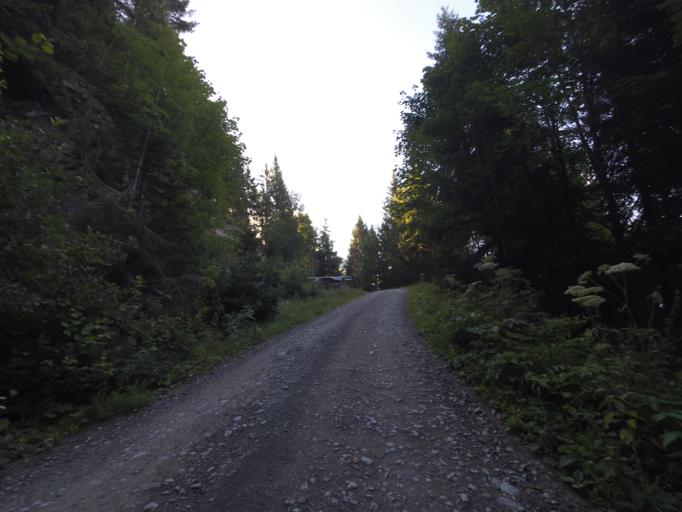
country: AT
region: Salzburg
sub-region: Politischer Bezirk Sankt Johann im Pongau
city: Goldegg
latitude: 47.3439
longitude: 13.1059
